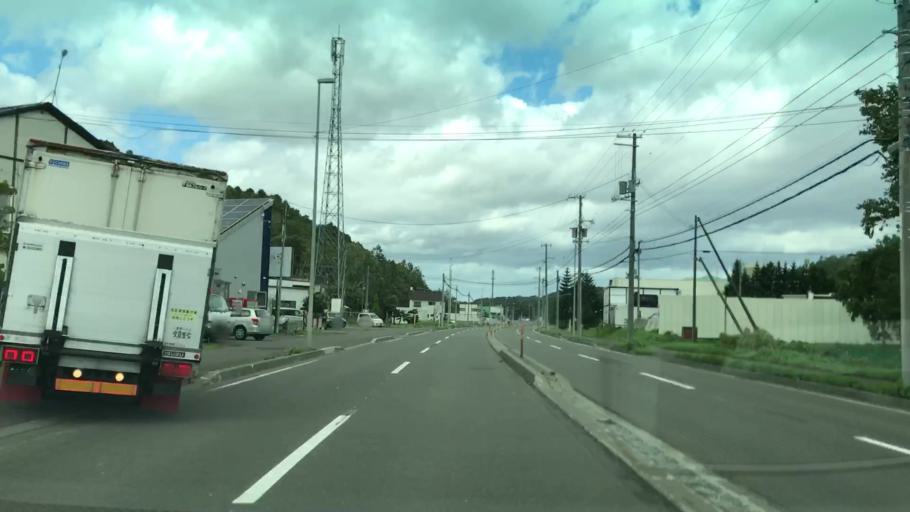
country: JP
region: Hokkaido
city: Kitahiroshima
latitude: 42.9695
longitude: 141.4534
